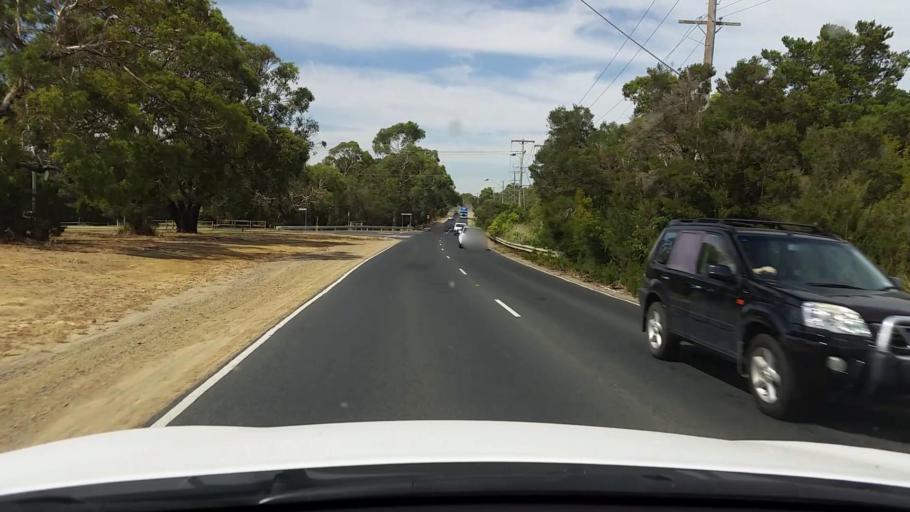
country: AU
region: Victoria
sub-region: Mornington Peninsula
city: Hastings
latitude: -38.3156
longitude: 145.1836
